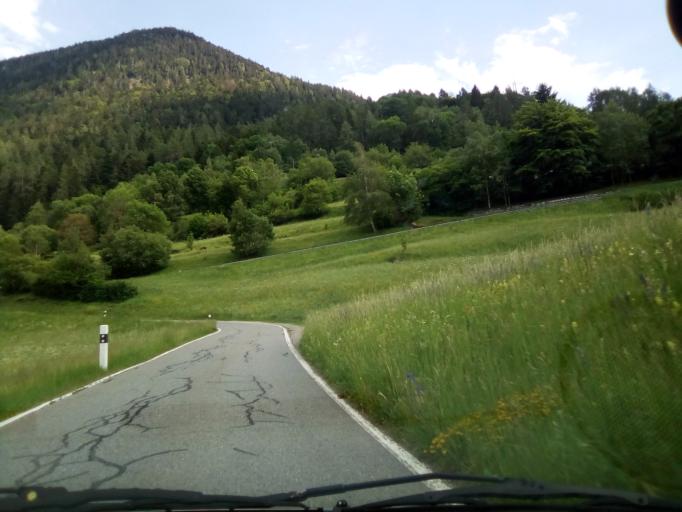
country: CH
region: Valais
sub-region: Entremont District
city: Orsieres
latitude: 46.0749
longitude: 7.1591
